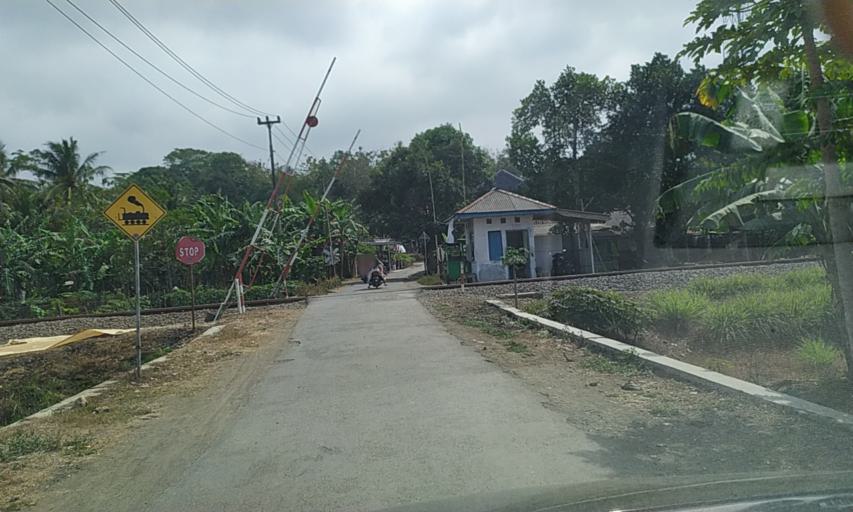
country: ID
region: Central Java
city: Sawoan
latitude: -7.6220
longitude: 109.0720
